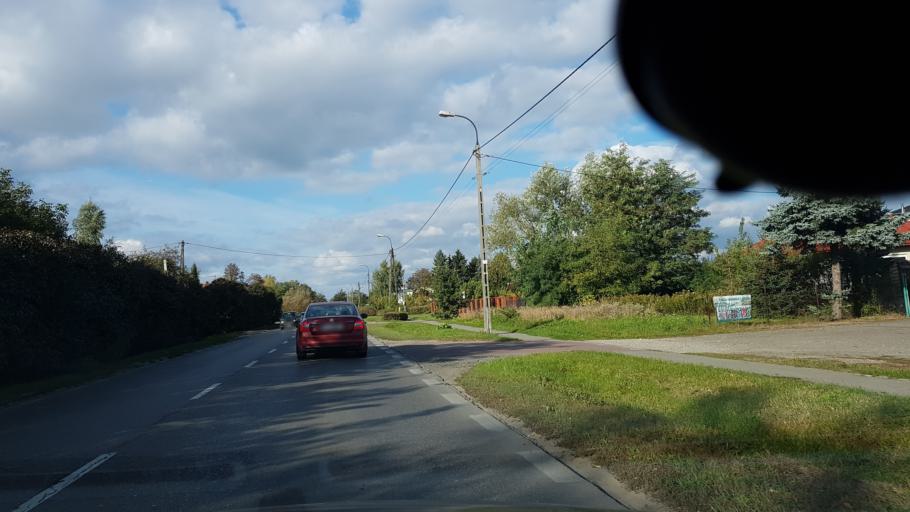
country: PL
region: Masovian Voivodeship
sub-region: Warszawa
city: Targowek
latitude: 52.3046
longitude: 21.0299
